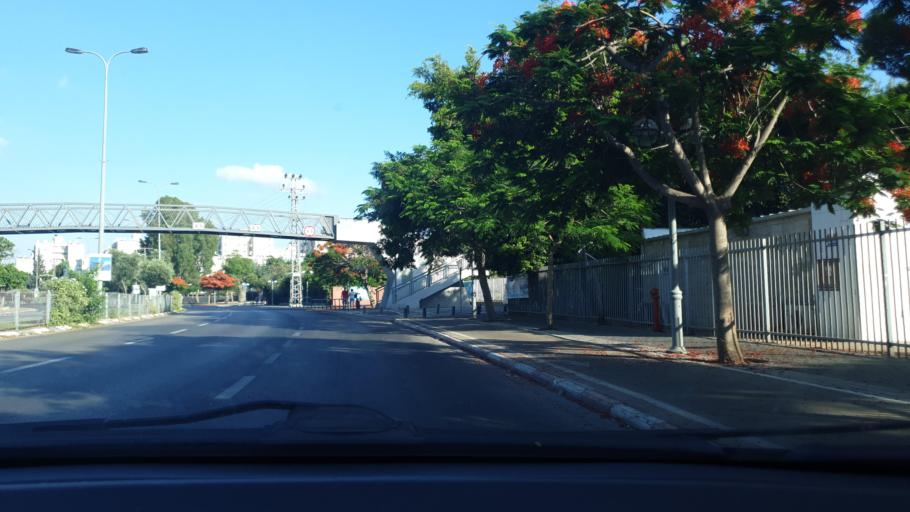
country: IL
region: Tel Aviv
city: Giv`atayim
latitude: 32.0578
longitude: 34.8043
